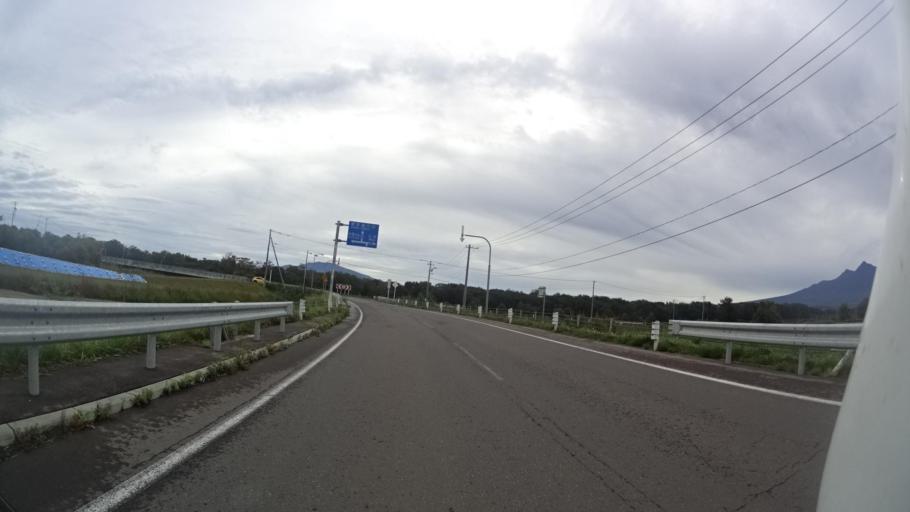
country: JP
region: Hokkaido
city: Abashiri
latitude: 43.8713
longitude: 144.6820
